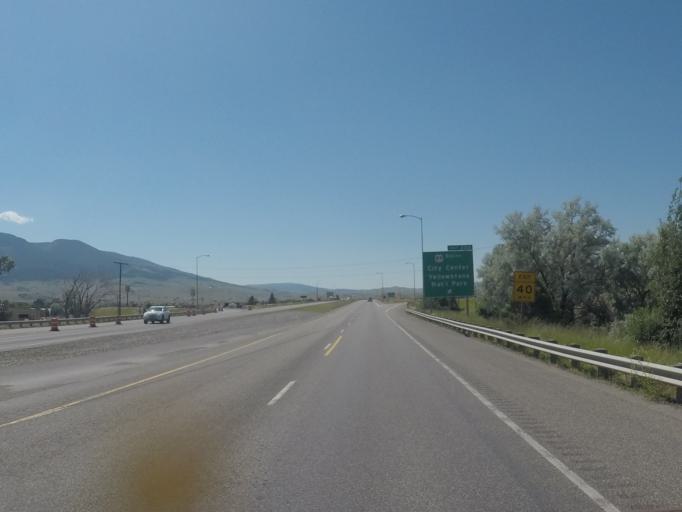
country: US
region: Montana
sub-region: Park County
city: Livingston
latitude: 45.6446
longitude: -110.5663
